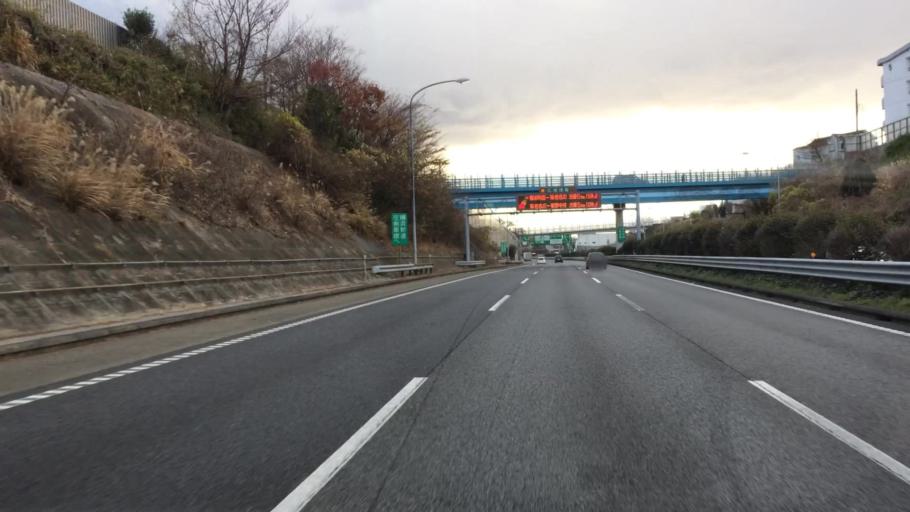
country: JP
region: Kanagawa
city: Yokohama
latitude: 35.4911
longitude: 139.5924
